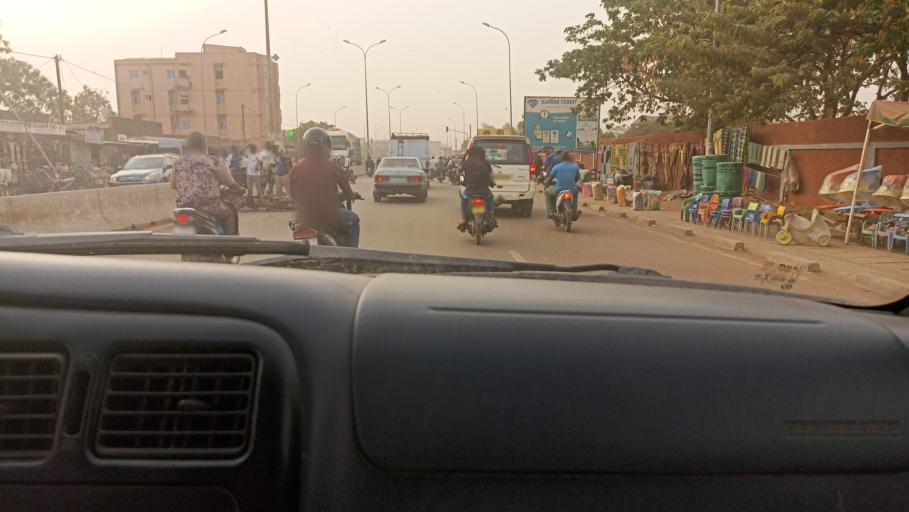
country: BF
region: Centre
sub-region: Kadiogo Province
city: Ouagadougou
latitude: 12.3803
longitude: -1.5492
